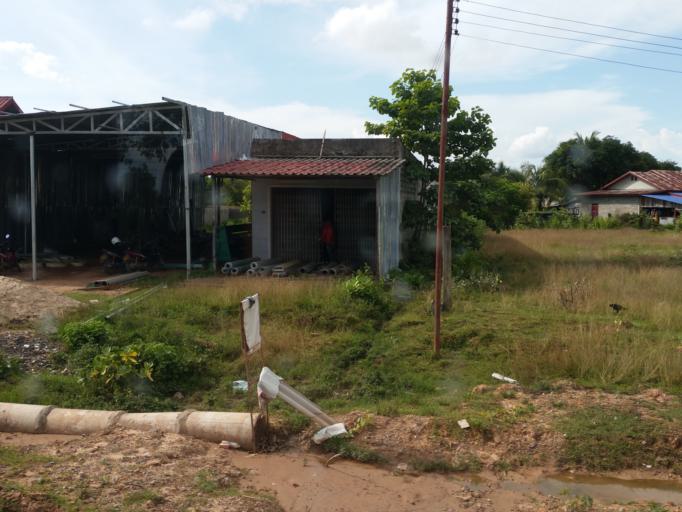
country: LA
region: Champasak
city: Pakxe
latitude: 15.1036
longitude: 105.7575
